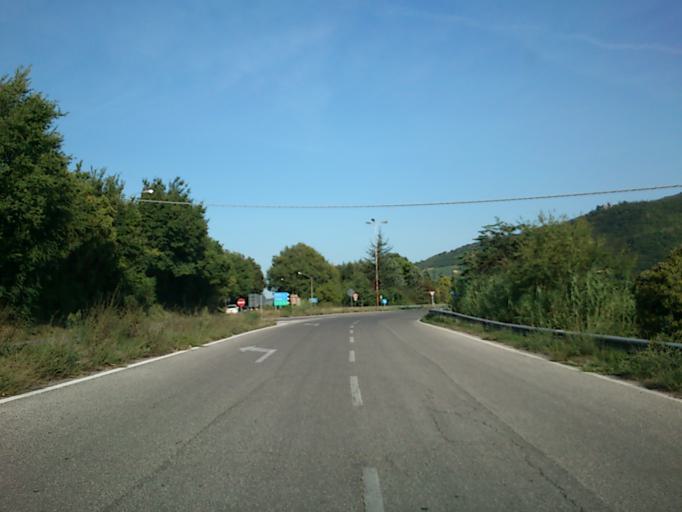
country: IT
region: The Marches
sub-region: Provincia di Pesaro e Urbino
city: Fossombrone
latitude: 43.6859
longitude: 12.7895
